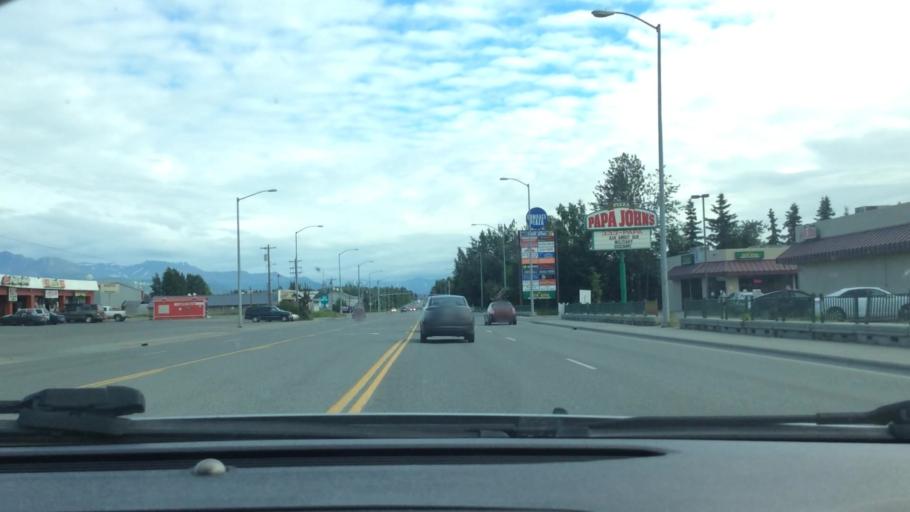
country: US
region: Alaska
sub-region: Anchorage Municipality
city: Anchorage
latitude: 61.2217
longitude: -149.7786
